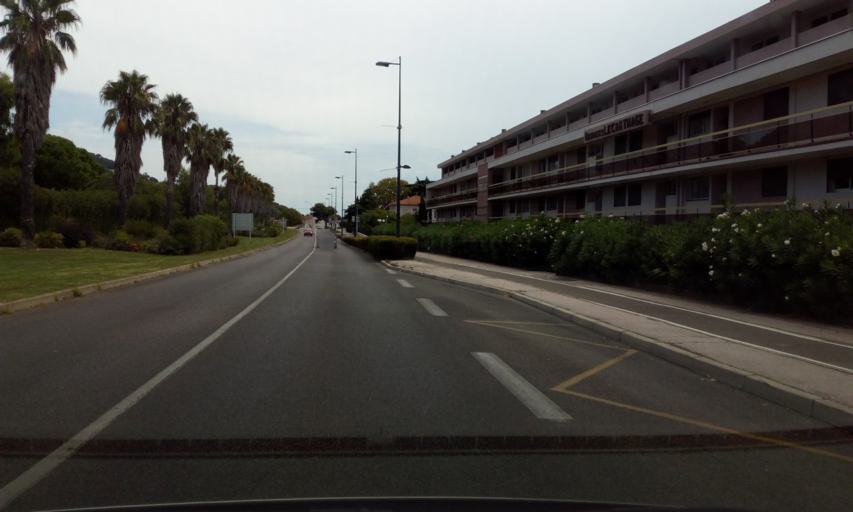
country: FR
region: Provence-Alpes-Cote d'Azur
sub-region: Departement du Var
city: Carqueiranne
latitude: 43.0911
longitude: 6.0810
